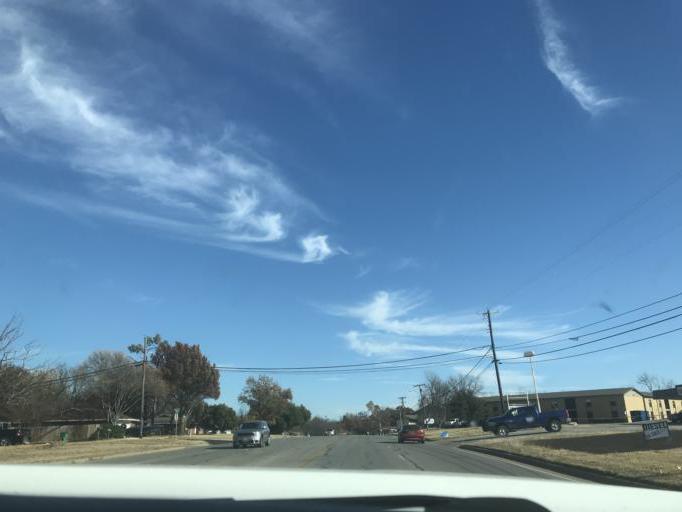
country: US
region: Texas
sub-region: Erath County
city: Stephenville
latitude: 32.2252
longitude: -98.2278
